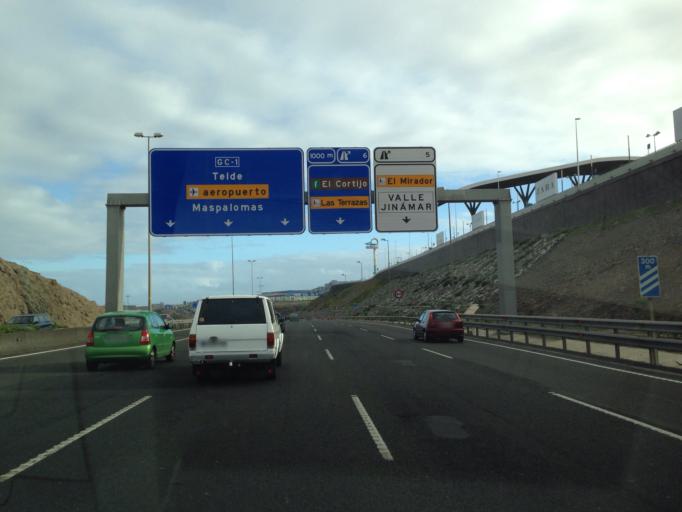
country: ES
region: Canary Islands
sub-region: Provincia de Las Palmas
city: Telde
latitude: 28.0343
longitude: -15.4037
